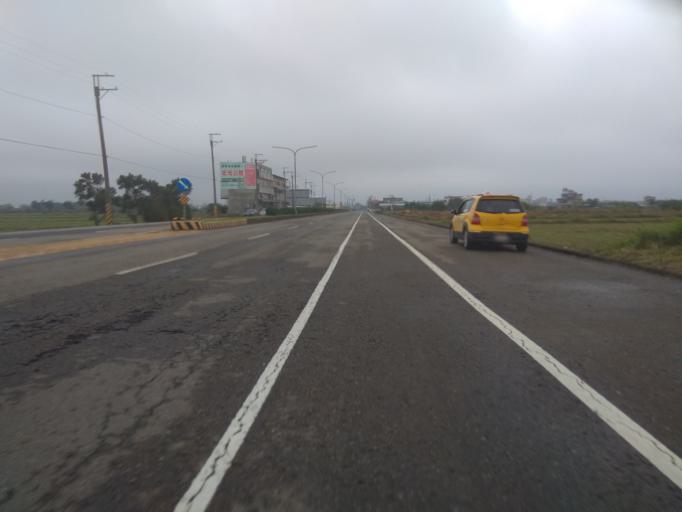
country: TW
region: Taiwan
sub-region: Hsinchu
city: Zhubei
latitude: 25.0253
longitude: 121.0808
